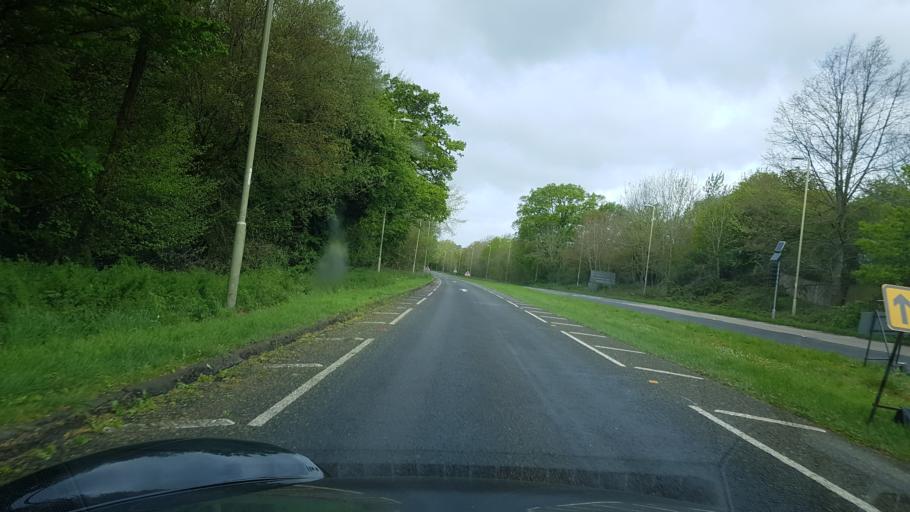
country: GB
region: England
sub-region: Hampshire
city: Kingsclere
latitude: 51.3278
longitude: -1.2396
